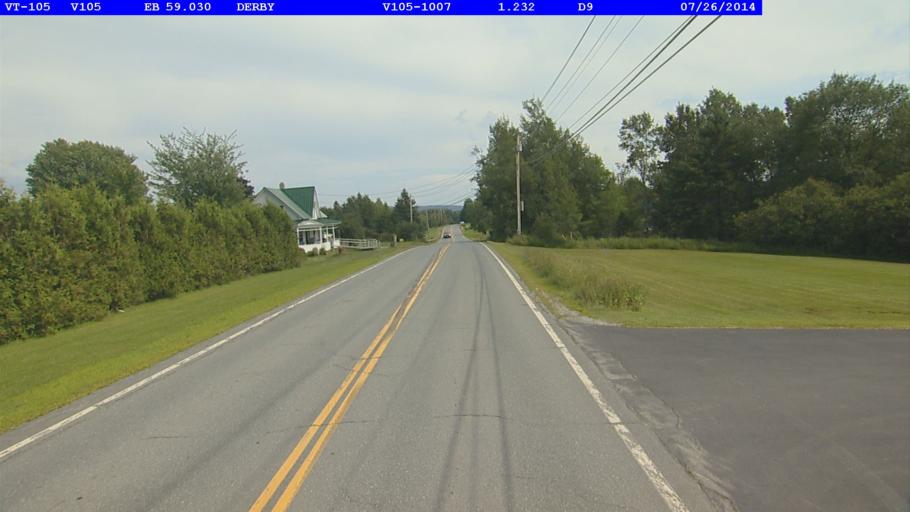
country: US
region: Vermont
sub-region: Orleans County
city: Newport
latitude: 44.9391
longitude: -72.1275
